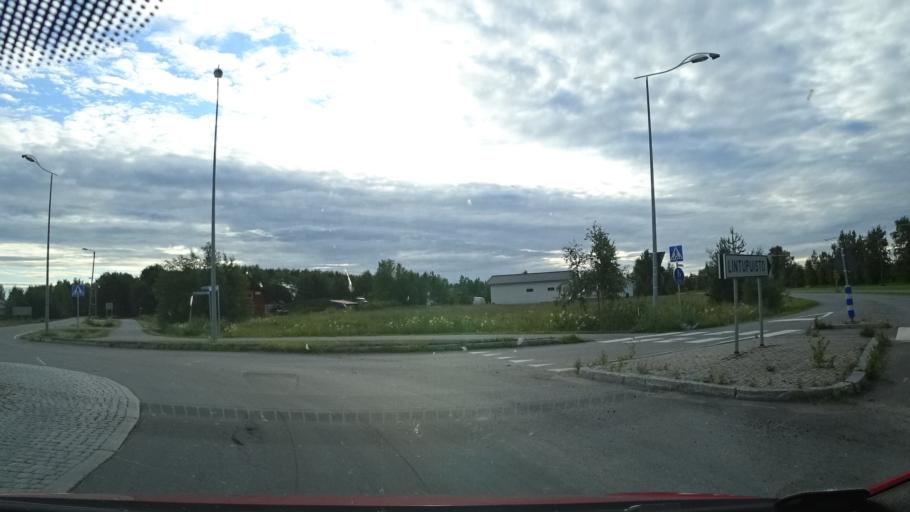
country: FI
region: Northern Ostrobothnia
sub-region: Oulu
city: Liminka
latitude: 64.8087
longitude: 25.4553
